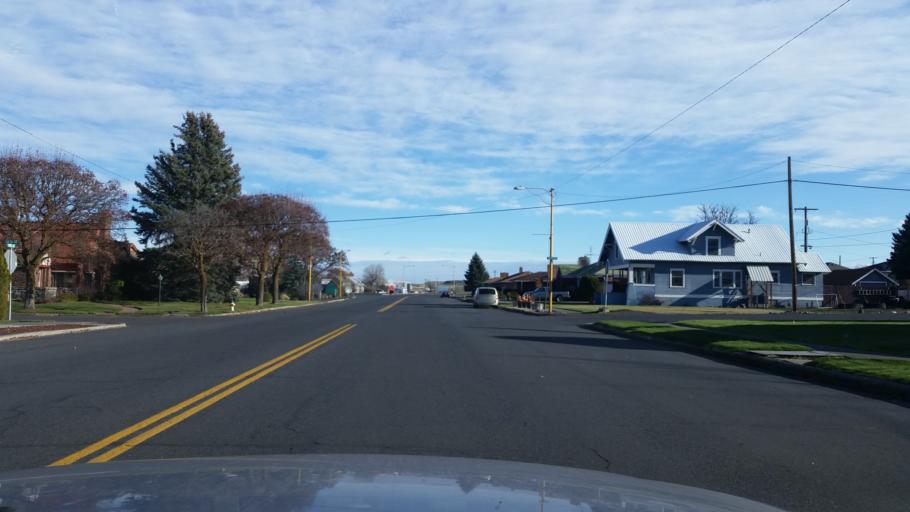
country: US
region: Washington
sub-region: Adams County
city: Ritzville
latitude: 47.3329
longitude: -118.6812
